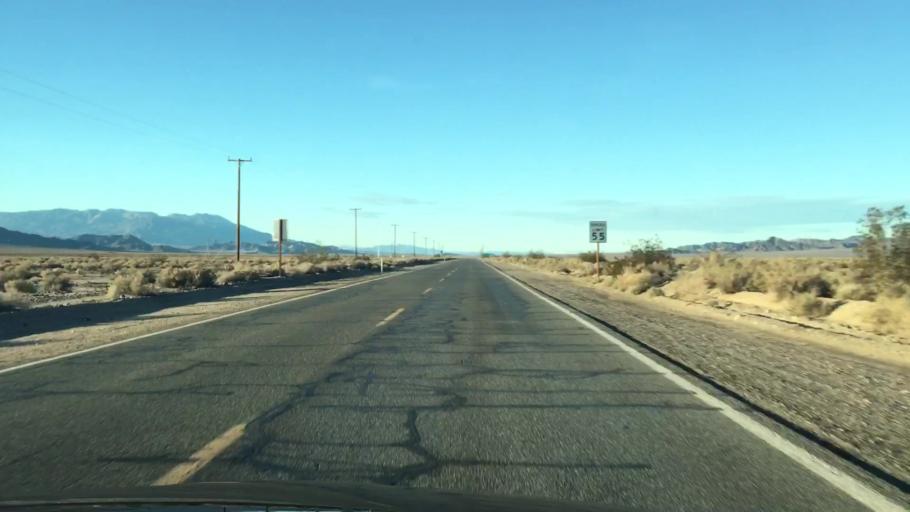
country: US
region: California
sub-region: San Bernardino County
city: Fort Irwin
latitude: 35.2817
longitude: -116.0771
